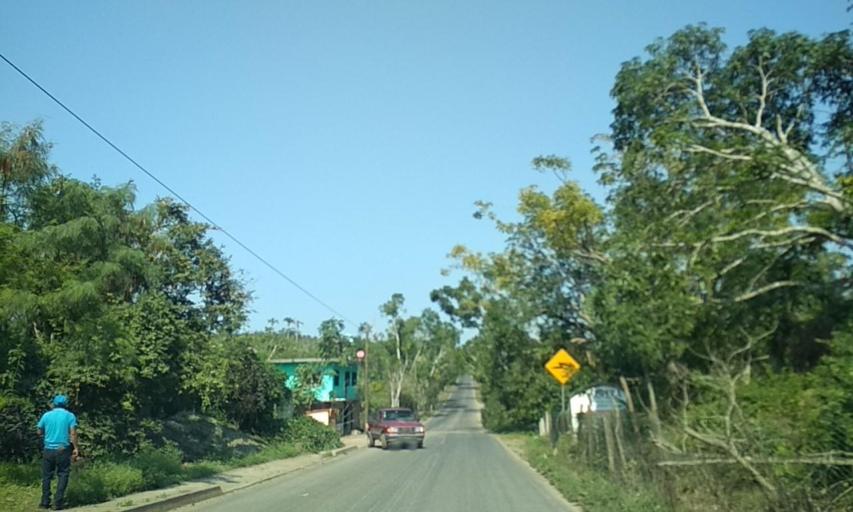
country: MX
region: Veracruz
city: Gutierrez Zamora
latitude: 20.3517
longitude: -97.1525
